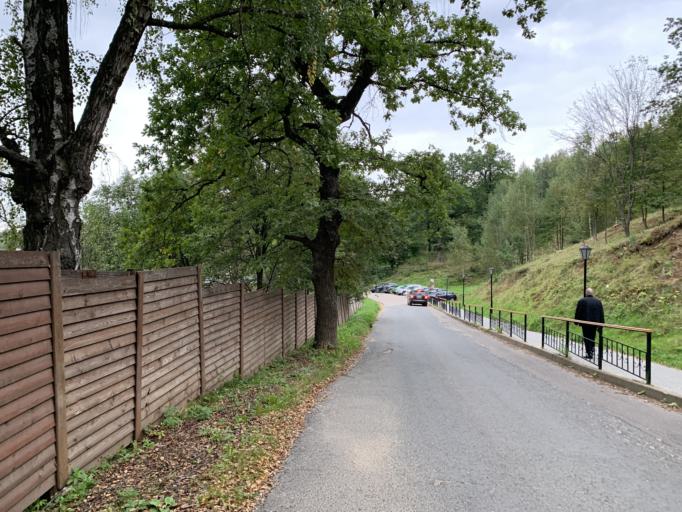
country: RU
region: Moskovskaya
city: Zvenigorod
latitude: 55.7343
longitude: 36.8110
